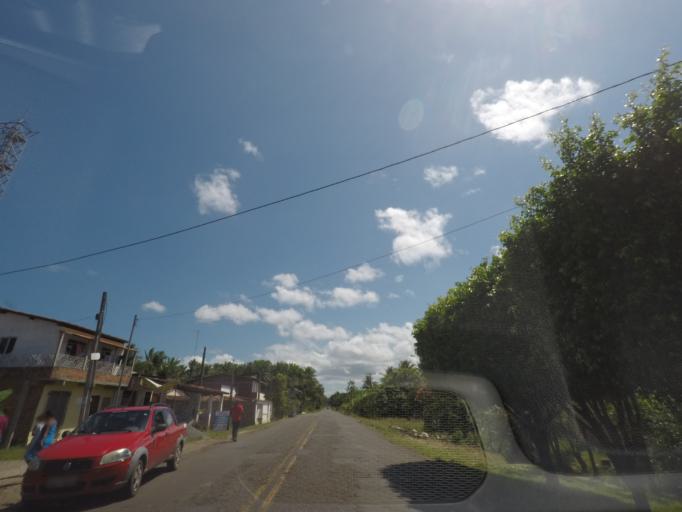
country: BR
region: Bahia
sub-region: Taperoa
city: Taperoa
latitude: -13.4830
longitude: -39.0910
